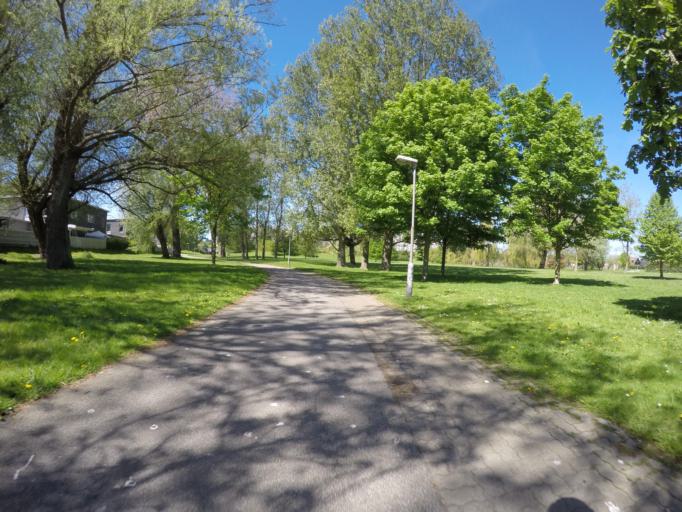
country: SE
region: Skane
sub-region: Burlovs Kommun
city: Arloev
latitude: 55.5895
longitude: 13.0586
